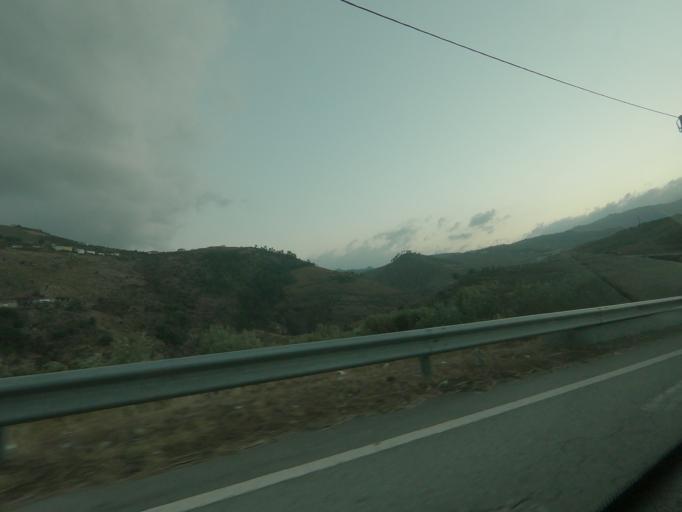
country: PT
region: Vila Real
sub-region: Peso da Regua
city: Peso da Regua
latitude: 41.1316
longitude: -7.7698
